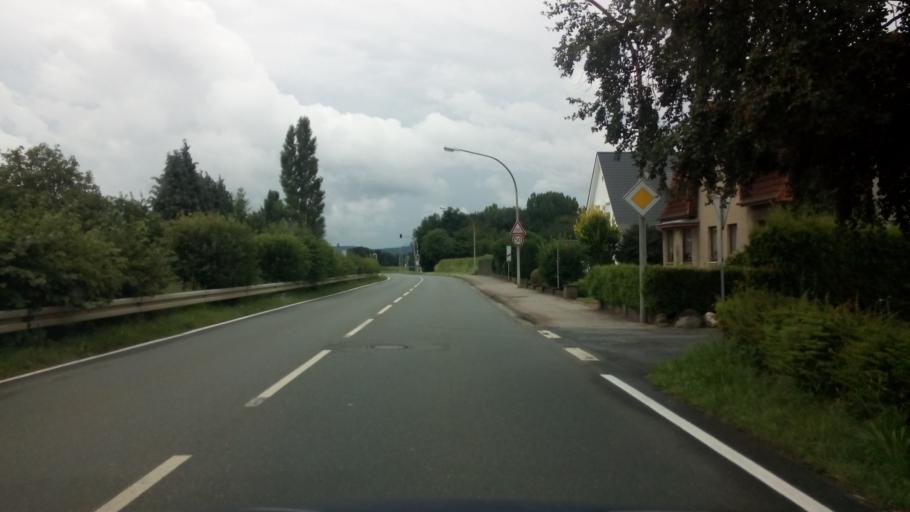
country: DE
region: Lower Saxony
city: Bohmte
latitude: 52.3557
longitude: 8.3105
